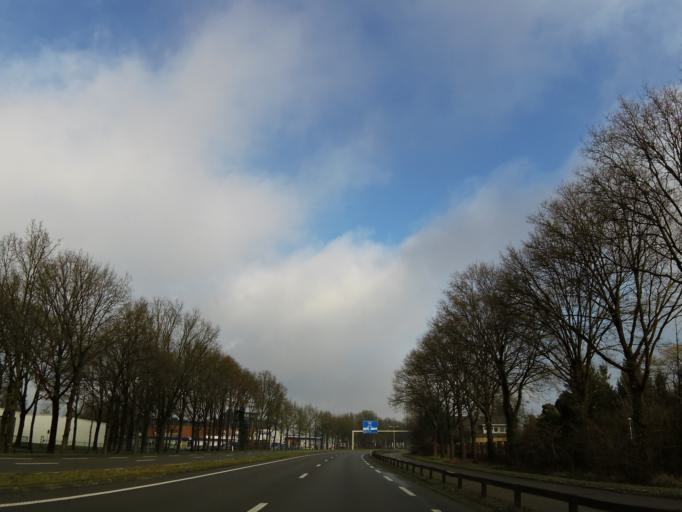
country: NL
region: Gelderland
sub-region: Gemeente Nijmegen
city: Lindenholt
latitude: 51.8151
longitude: 5.7649
